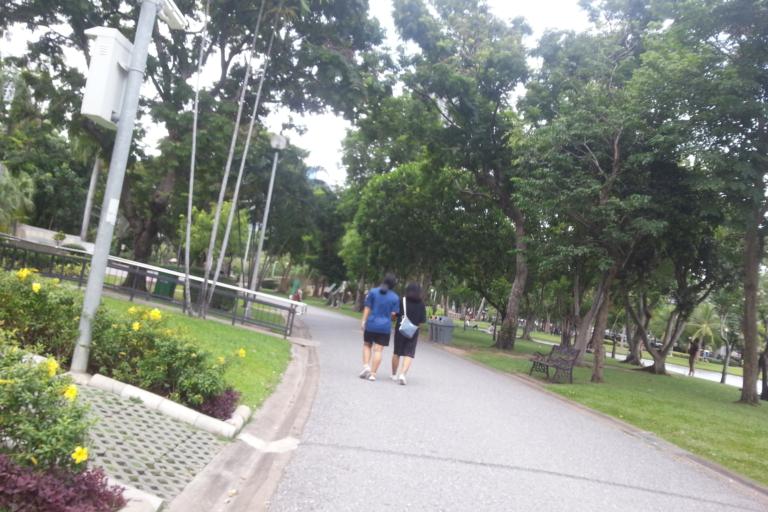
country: TH
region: Bangkok
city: Bang Sue
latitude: 13.8042
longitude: 100.5531
